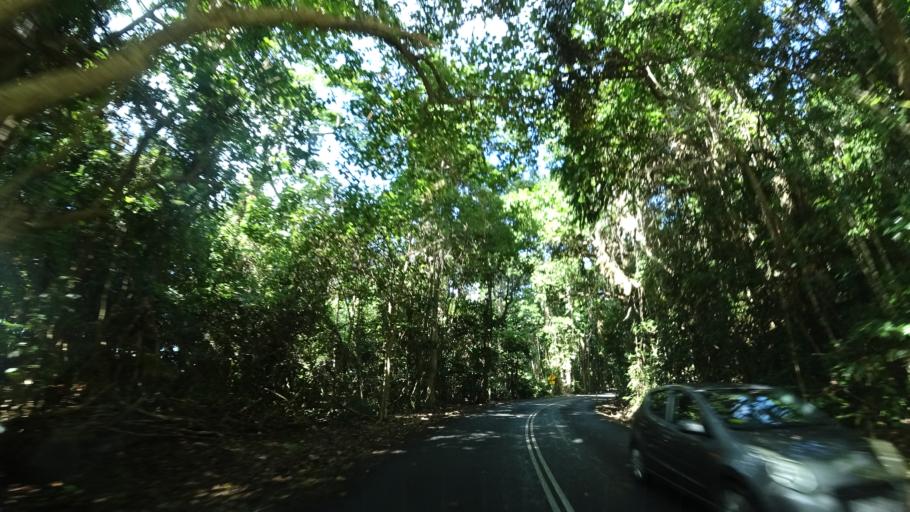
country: AU
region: Queensland
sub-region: Cairns
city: Port Douglas
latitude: -16.1121
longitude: 145.4571
